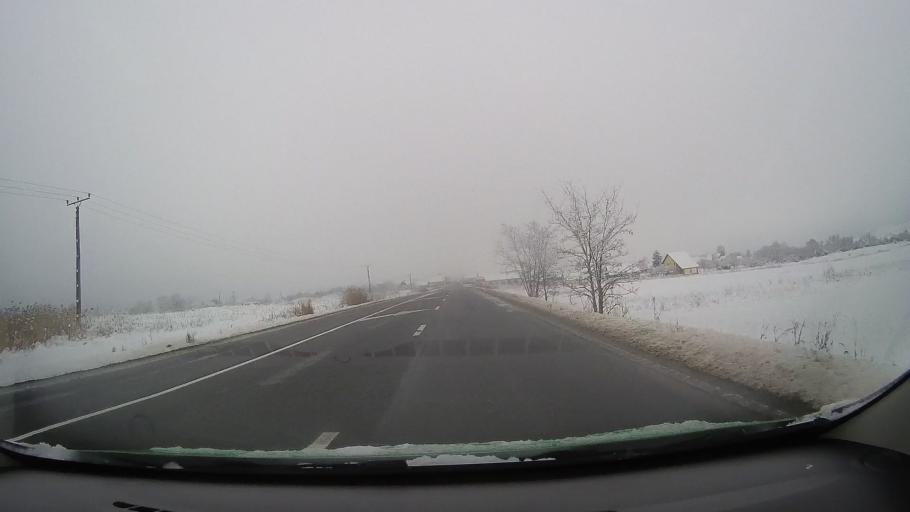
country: RO
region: Sibiu
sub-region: Oras Saliste
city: Saliste
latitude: 45.7872
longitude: 23.9312
